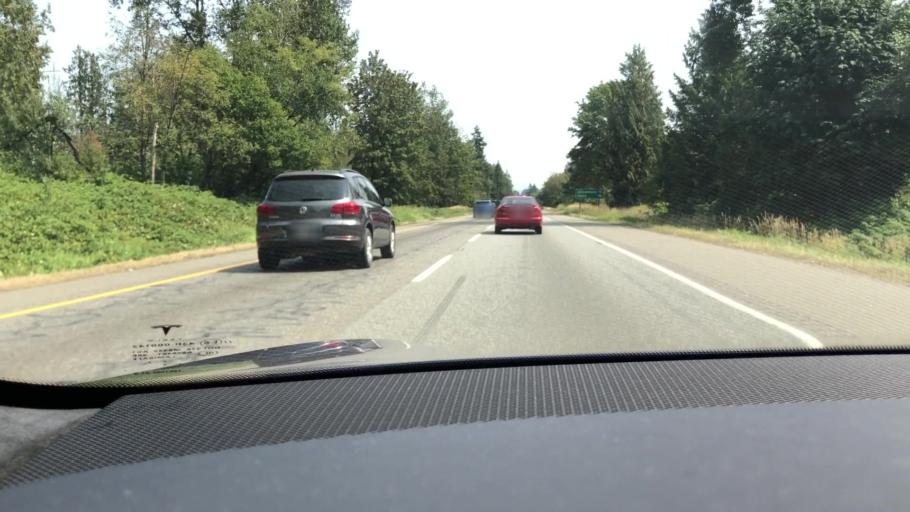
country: CA
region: British Columbia
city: Aldergrove
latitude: 49.0968
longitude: -122.4814
